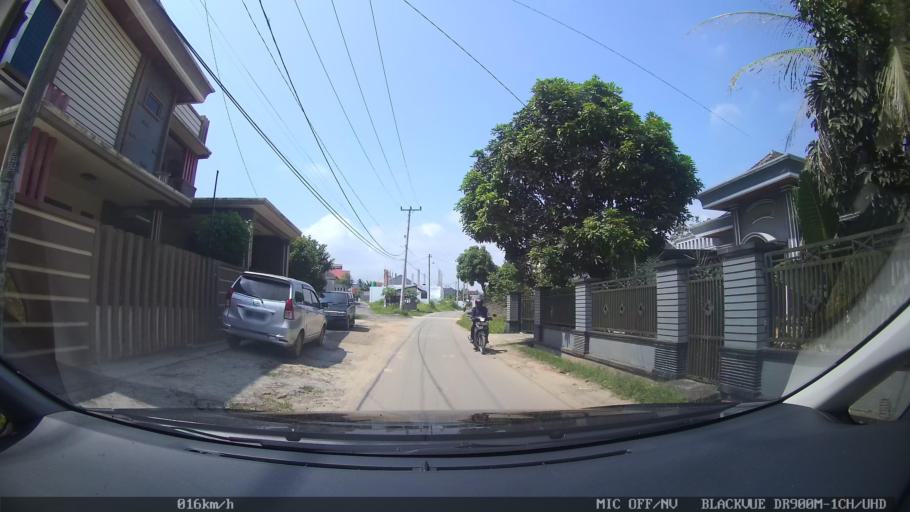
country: ID
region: Lampung
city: Kedaton
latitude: -5.3507
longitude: 105.2760
